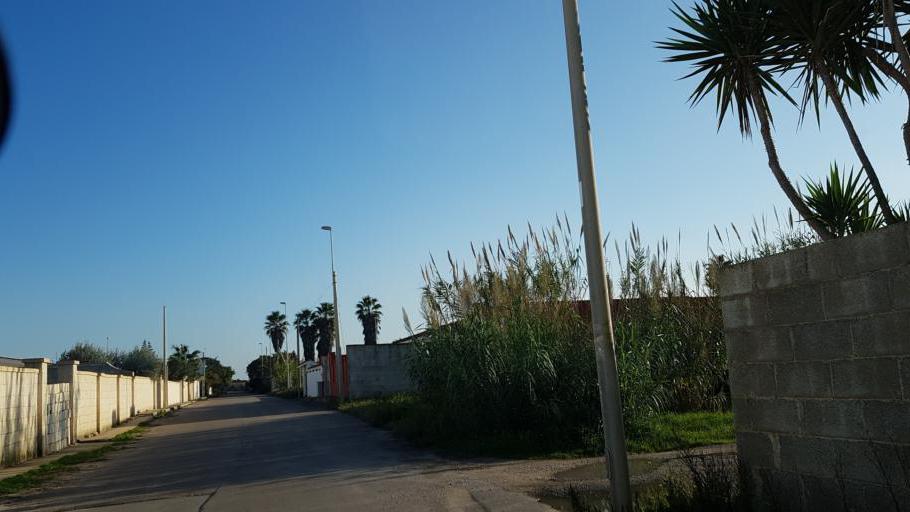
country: IT
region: Apulia
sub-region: Provincia di Brindisi
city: Torchiarolo
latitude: 40.5143
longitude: 18.0971
